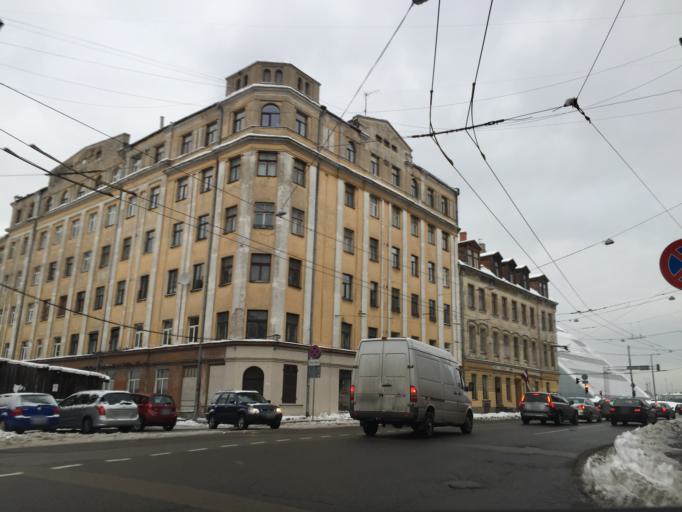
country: LV
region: Riga
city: Riga
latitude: 56.9394
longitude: 24.0964
